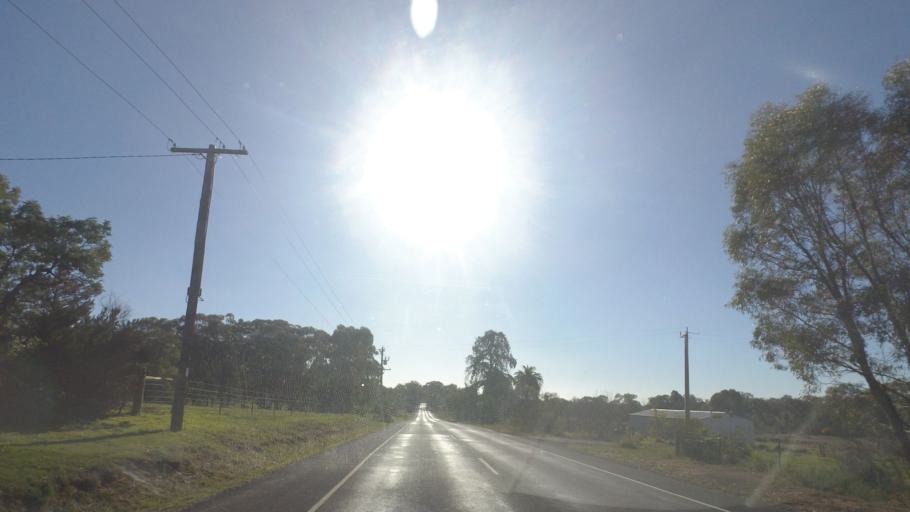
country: AU
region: Victoria
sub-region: Greater Bendigo
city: Kennington
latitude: -36.8970
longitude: 144.3141
